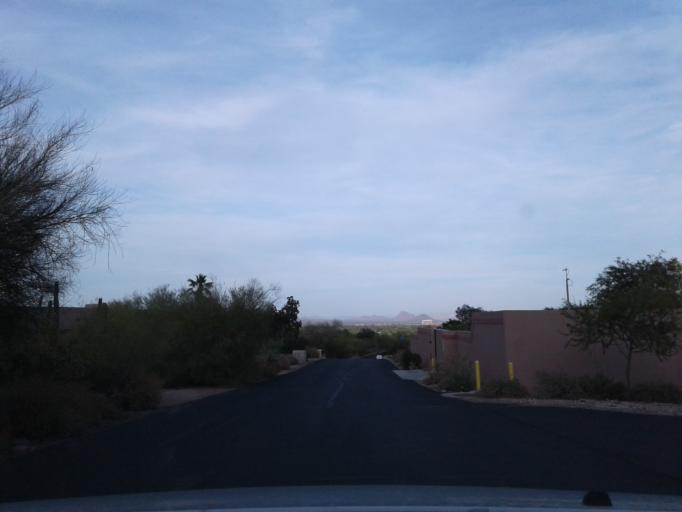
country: US
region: Arizona
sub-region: Maricopa County
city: Paradise Valley
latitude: 33.5457
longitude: -111.9514
